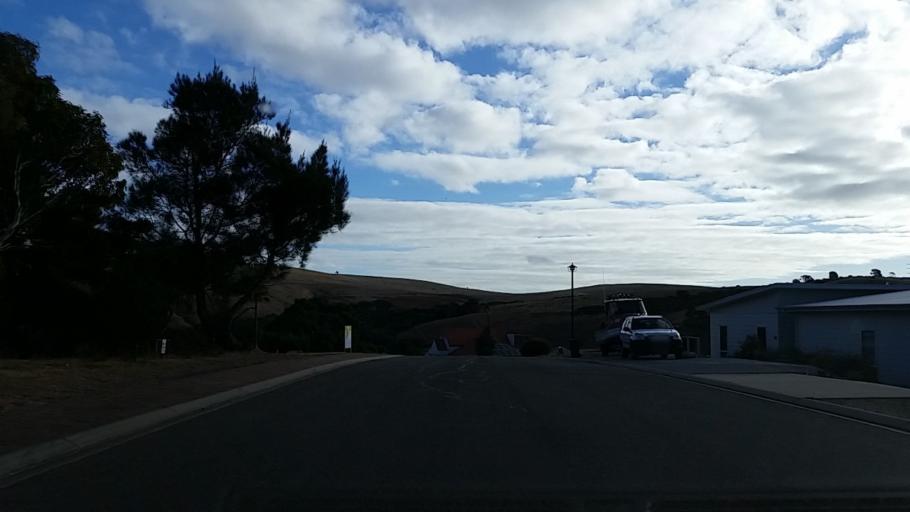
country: AU
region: South Australia
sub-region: Yankalilla
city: Normanville
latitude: -35.5045
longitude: 138.2468
